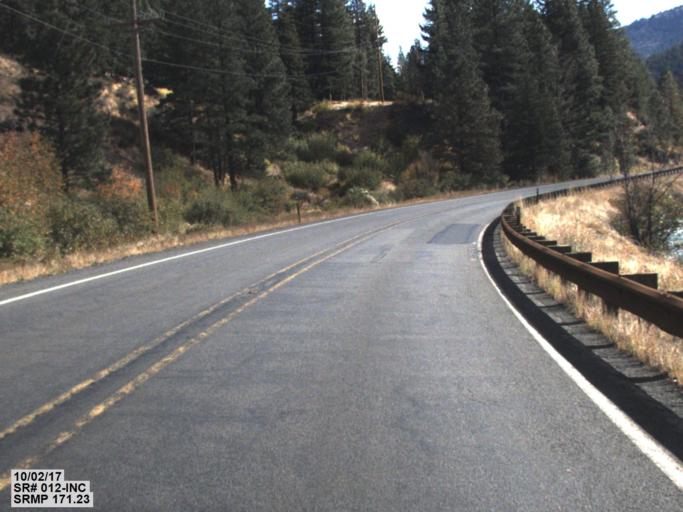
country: US
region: Washington
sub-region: Yakima County
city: Tieton
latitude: 46.6724
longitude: -121.0207
